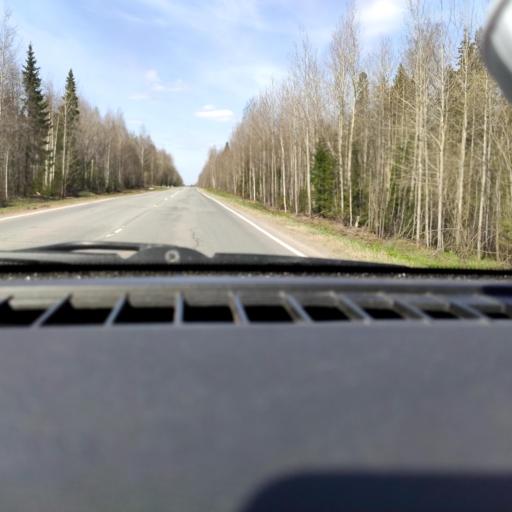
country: RU
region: Perm
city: Polazna
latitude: 58.2773
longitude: 56.1657
